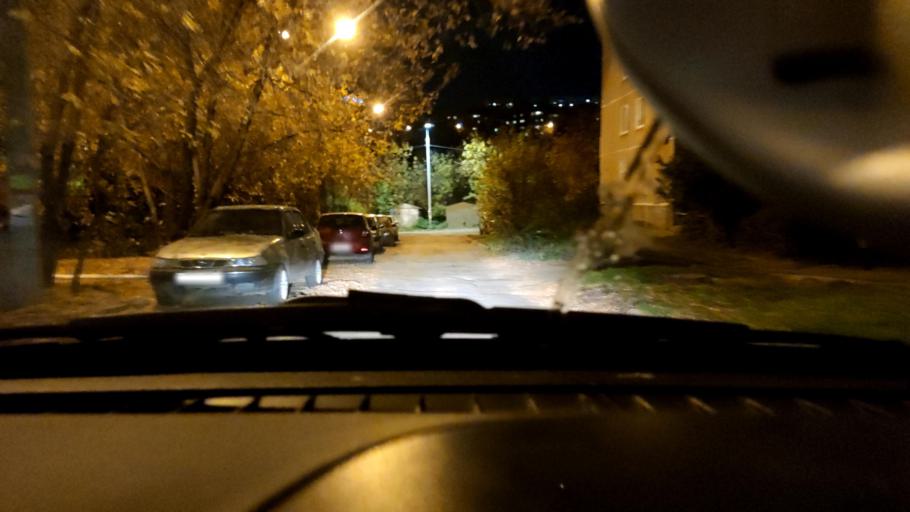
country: RU
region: Perm
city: Perm
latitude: 57.9953
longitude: 56.2303
